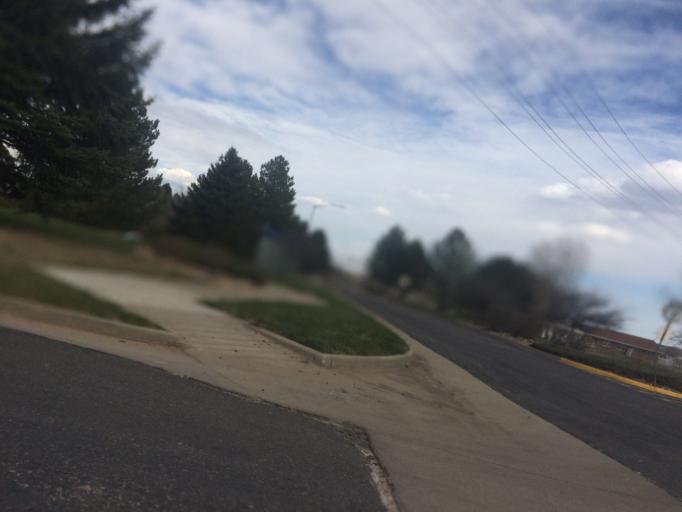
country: US
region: Colorado
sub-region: Boulder County
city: Superior
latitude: 39.9510
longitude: -105.1489
